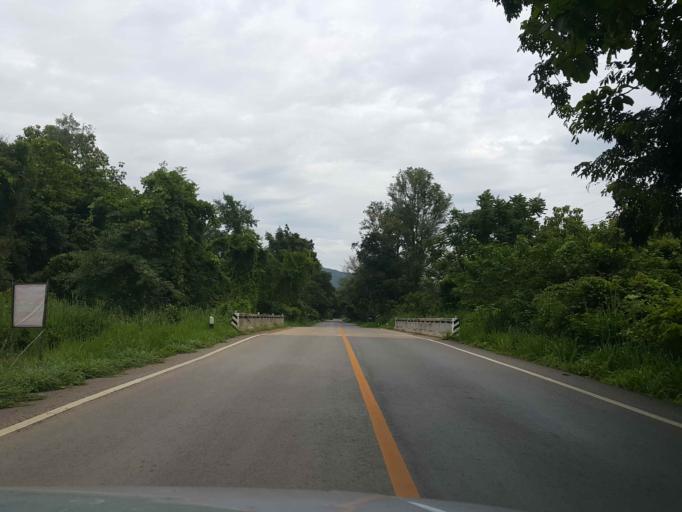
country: TH
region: Lampang
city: Thoen
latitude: 17.5654
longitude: 99.3311
